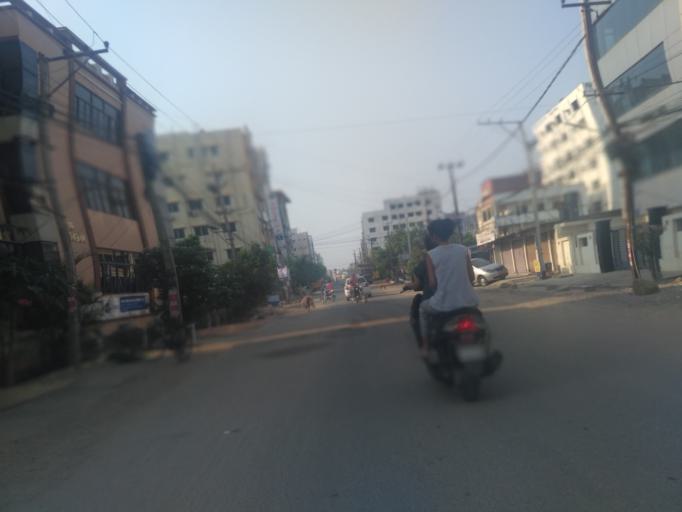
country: IN
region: Telangana
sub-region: Rangareddi
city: Kukatpalli
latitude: 17.4509
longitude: 78.3917
